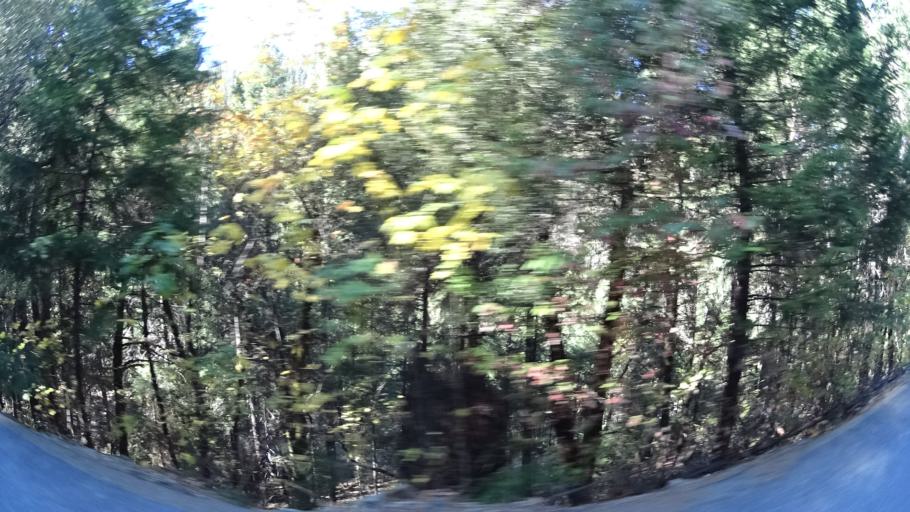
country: US
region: California
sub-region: Siskiyou County
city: Yreka
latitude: 41.3533
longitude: -123.0369
